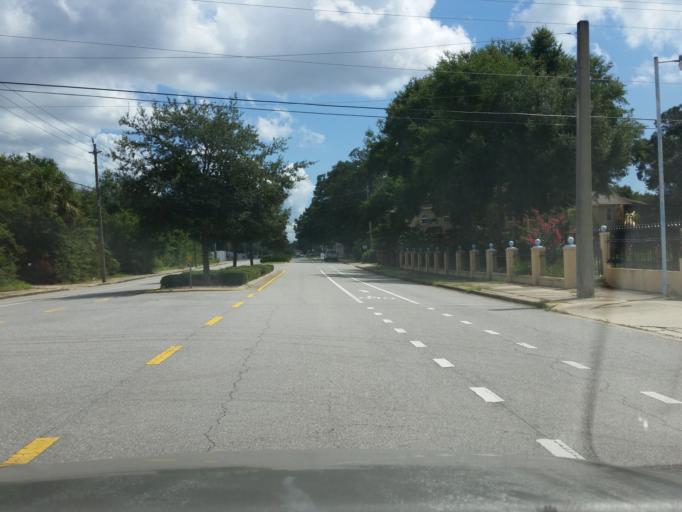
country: US
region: Florida
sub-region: Escambia County
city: Warrington
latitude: 30.3953
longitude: -87.2504
